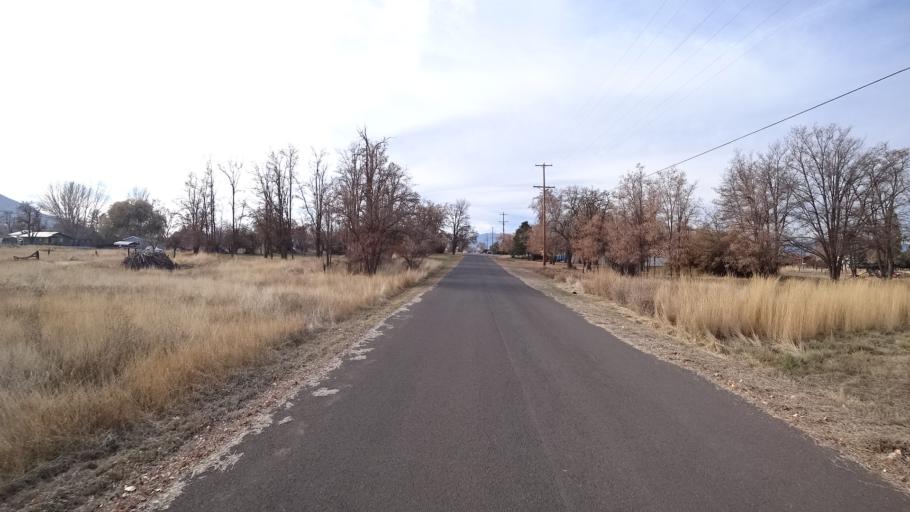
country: US
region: California
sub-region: Siskiyou County
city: Montague
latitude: 41.7313
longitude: -122.5321
